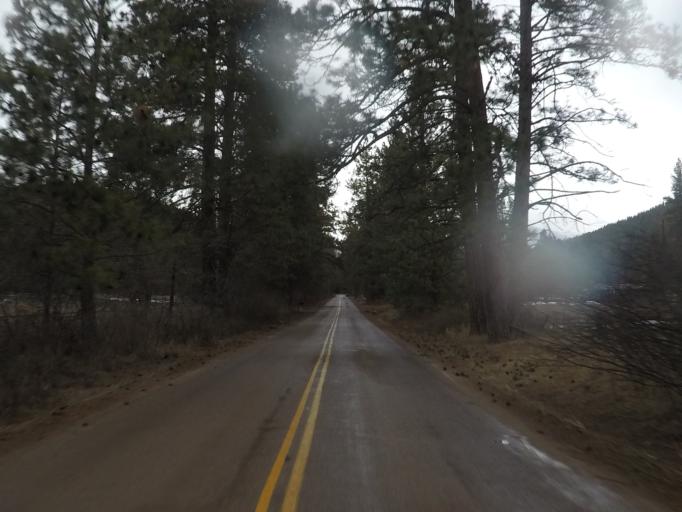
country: US
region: Montana
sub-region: Missoula County
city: East Missoula
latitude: 46.9144
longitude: -113.9603
